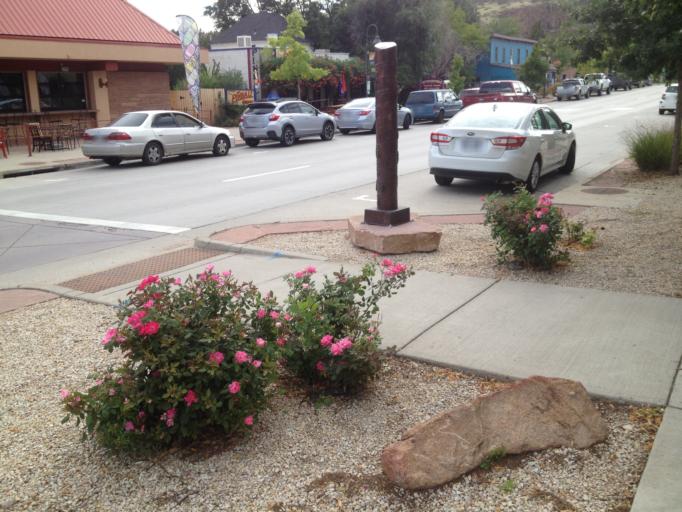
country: US
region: Colorado
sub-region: Boulder County
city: Lyons
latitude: 40.2248
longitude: -105.2684
